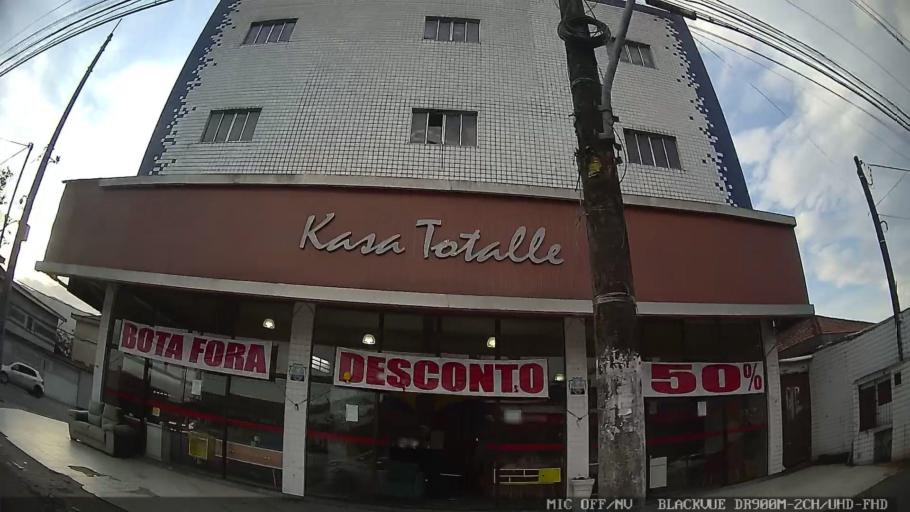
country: BR
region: Sao Paulo
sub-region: Cubatao
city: Cubatao
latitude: -23.8932
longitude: -46.4308
